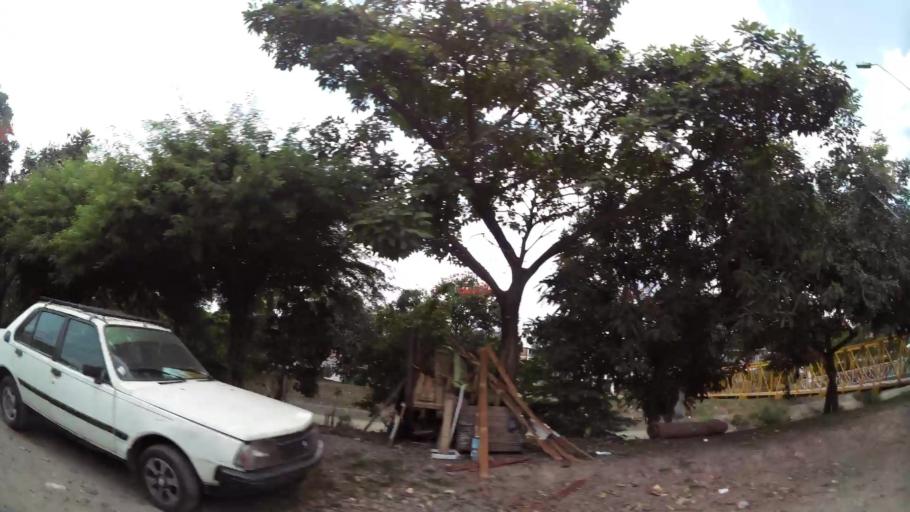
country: CO
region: Valle del Cauca
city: Cali
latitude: 3.4740
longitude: -76.4817
